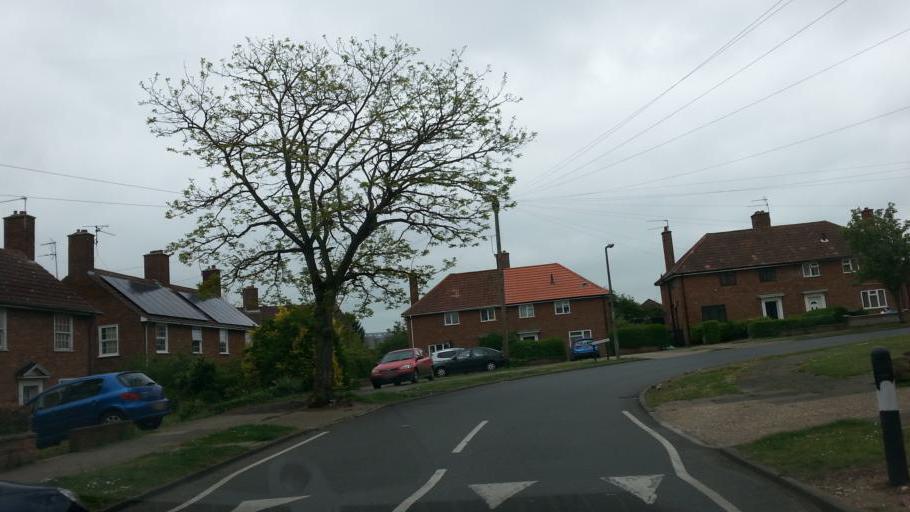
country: GB
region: England
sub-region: Suffolk
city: Bury St Edmunds
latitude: 52.2633
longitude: 0.7069
